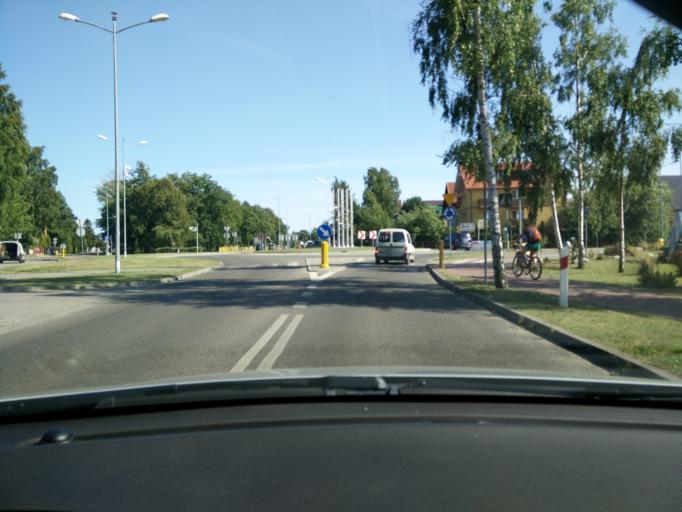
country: PL
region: Pomeranian Voivodeship
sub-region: Powiat pucki
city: Jastarnia
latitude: 54.7065
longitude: 18.6572
